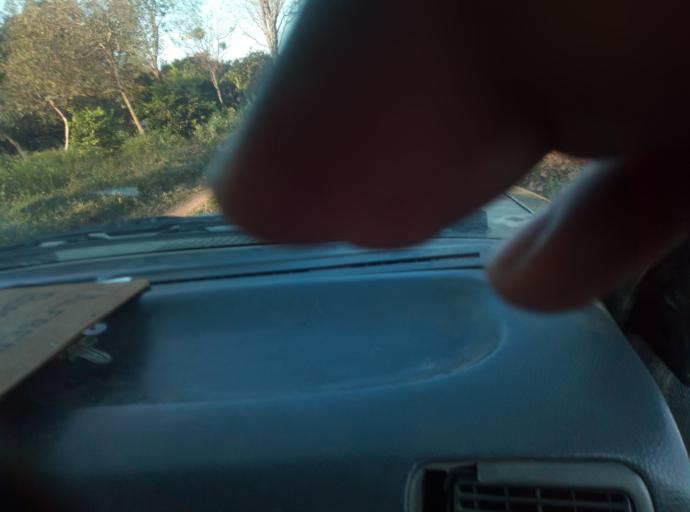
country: PY
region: Caaguazu
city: Doctor Cecilio Baez
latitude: -25.1517
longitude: -56.2499
